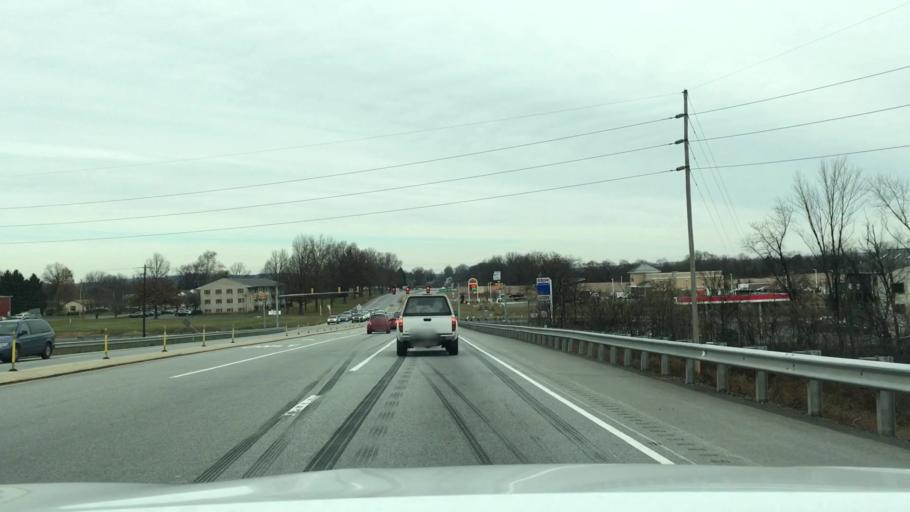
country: US
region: Pennsylvania
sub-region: Berks County
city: Boyertown
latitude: 40.3093
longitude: -75.6358
